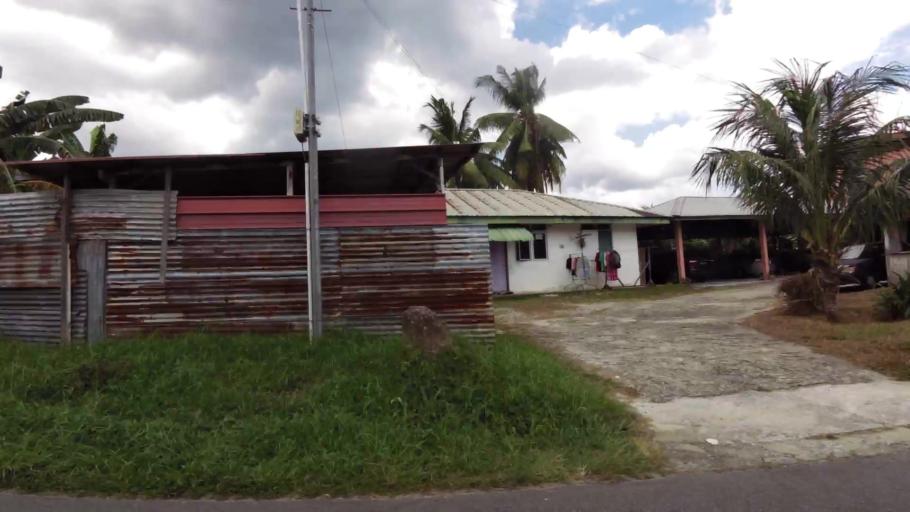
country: BN
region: Brunei and Muara
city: Bandar Seri Begawan
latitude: 4.9534
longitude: 114.9642
